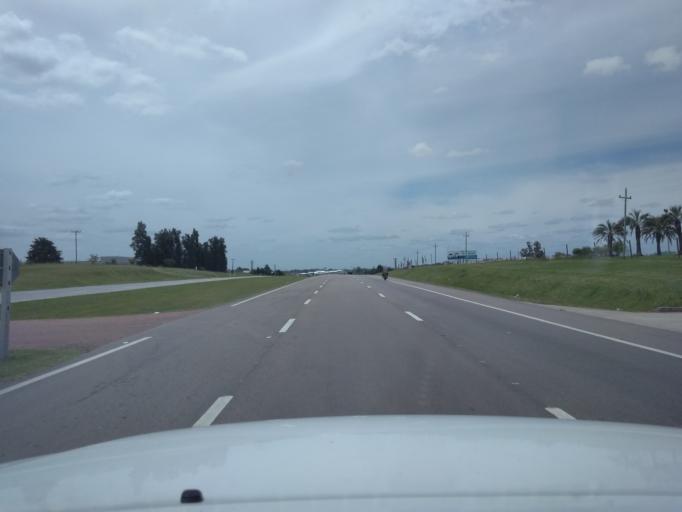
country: UY
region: Canelones
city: Las Piedras
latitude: -34.7047
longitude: -56.2408
